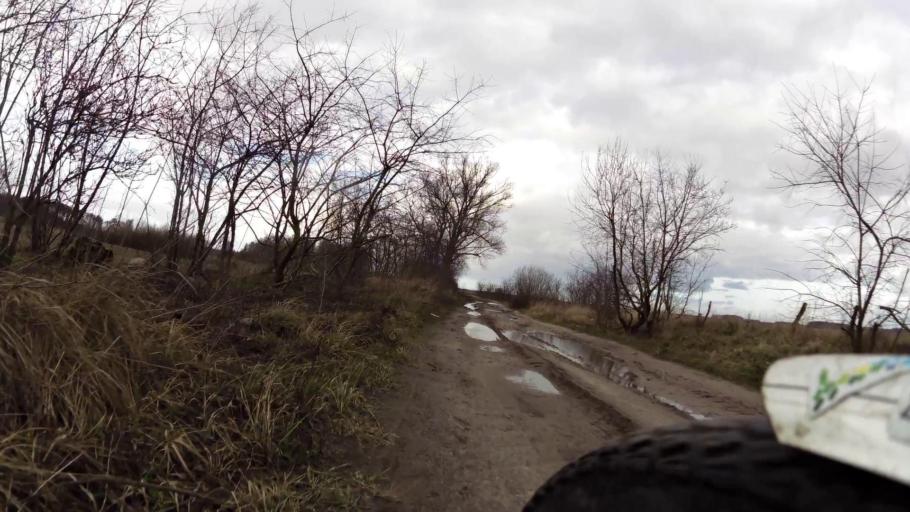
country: PL
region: West Pomeranian Voivodeship
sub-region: Powiat kamienski
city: Kamien Pomorski
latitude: 53.8825
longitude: 14.7163
